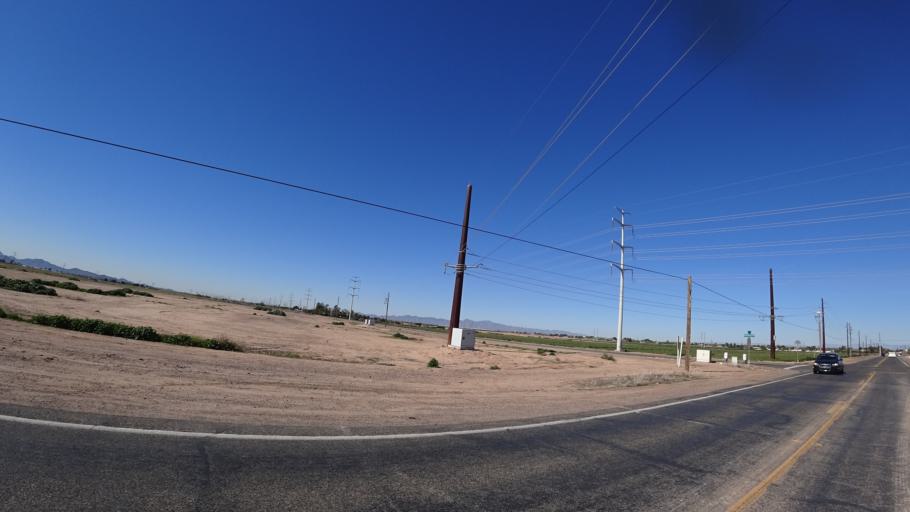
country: US
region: Arizona
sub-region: Maricopa County
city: Tolleson
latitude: 33.4059
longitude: -112.2893
